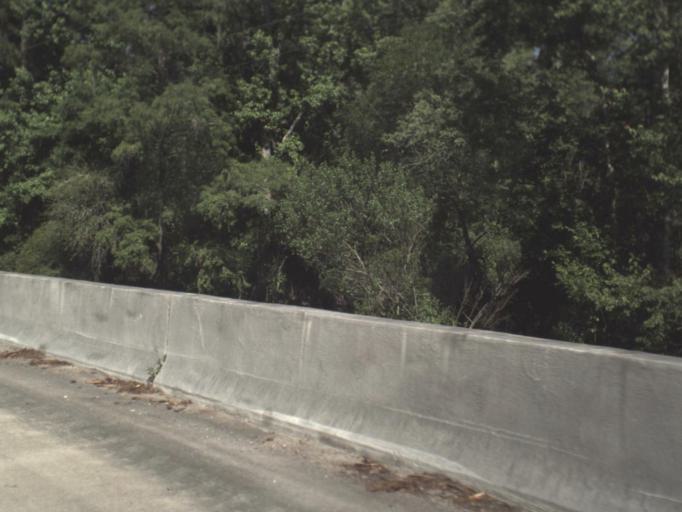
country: US
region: Florida
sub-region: Duval County
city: Baldwin
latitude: 30.3005
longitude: -82.0303
